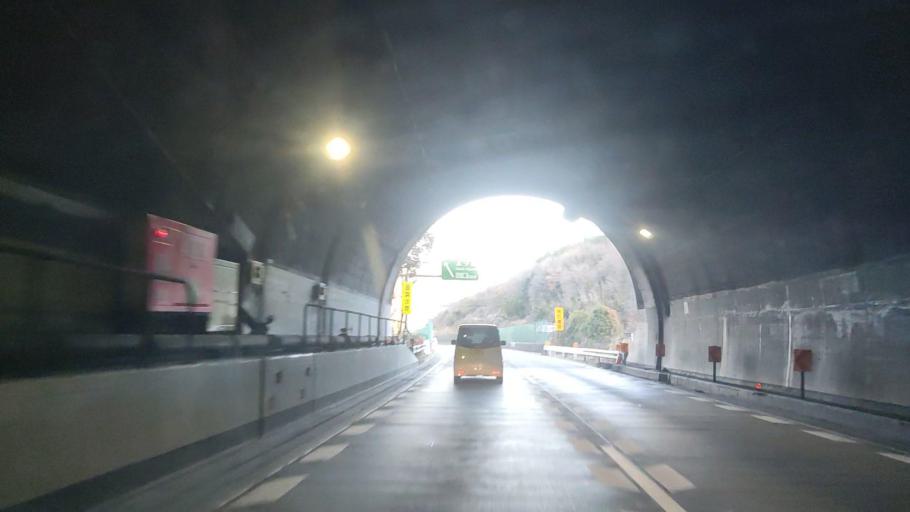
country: JP
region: Hyogo
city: Tatsunocho-tominaga
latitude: 34.8371
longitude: 134.6152
